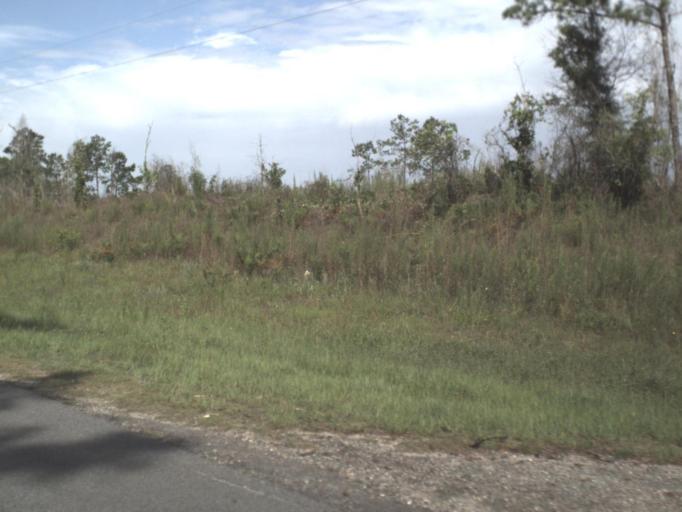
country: US
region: Florida
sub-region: Madison County
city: Madison
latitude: 30.6220
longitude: -83.3247
